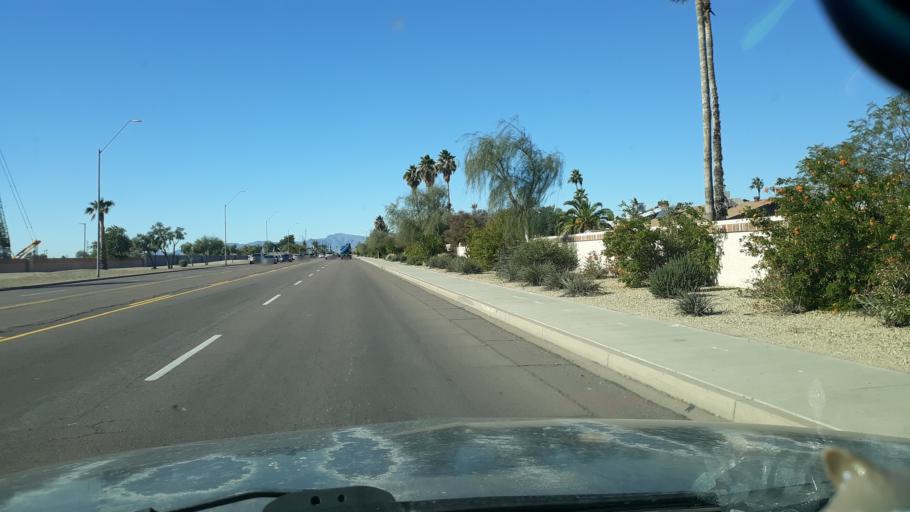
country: US
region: Arizona
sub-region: Maricopa County
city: Youngtown
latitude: 33.5512
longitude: -112.2848
